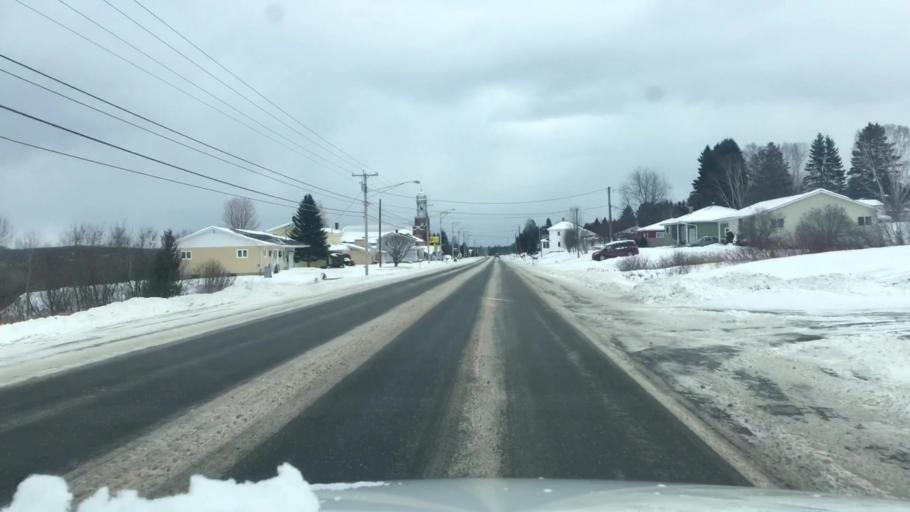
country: US
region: Maine
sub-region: Aroostook County
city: Madawaska
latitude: 47.3497
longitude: -68.2824
